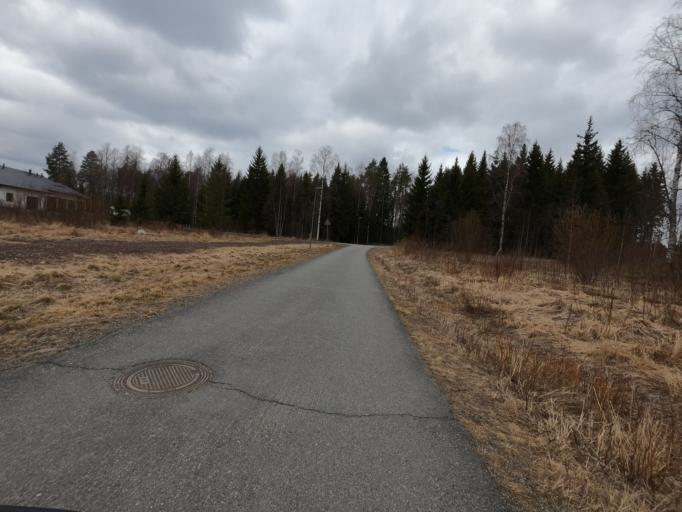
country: FI
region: North Karelia
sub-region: Joensuu
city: Joensuu
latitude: 62.5689
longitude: 29.8144
